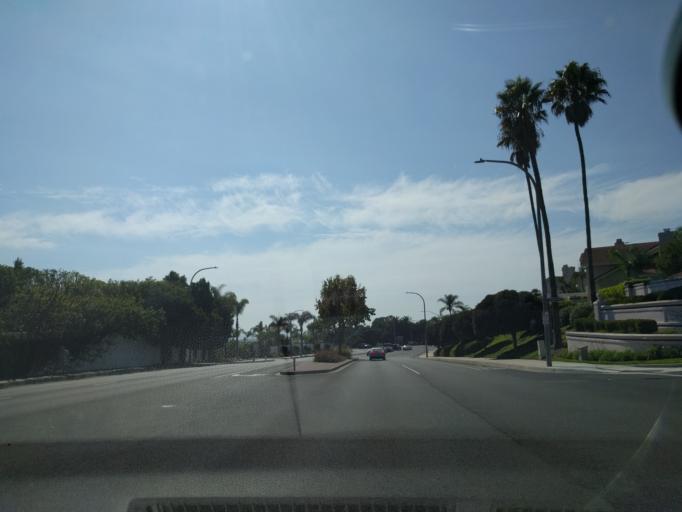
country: US
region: California
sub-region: Orange County
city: San Joaquin Hills
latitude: 33.6117
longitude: -117.8679
